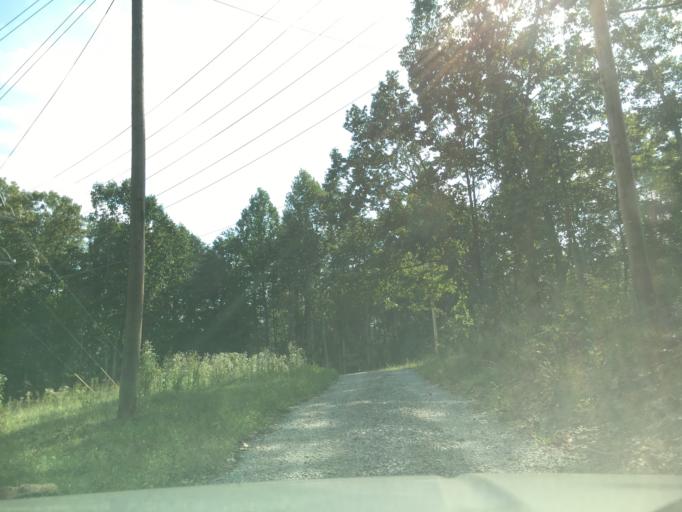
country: US
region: Virginia
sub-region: City of Lynchburg
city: West Lynchburg
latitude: 37.3337
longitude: -79.1815
